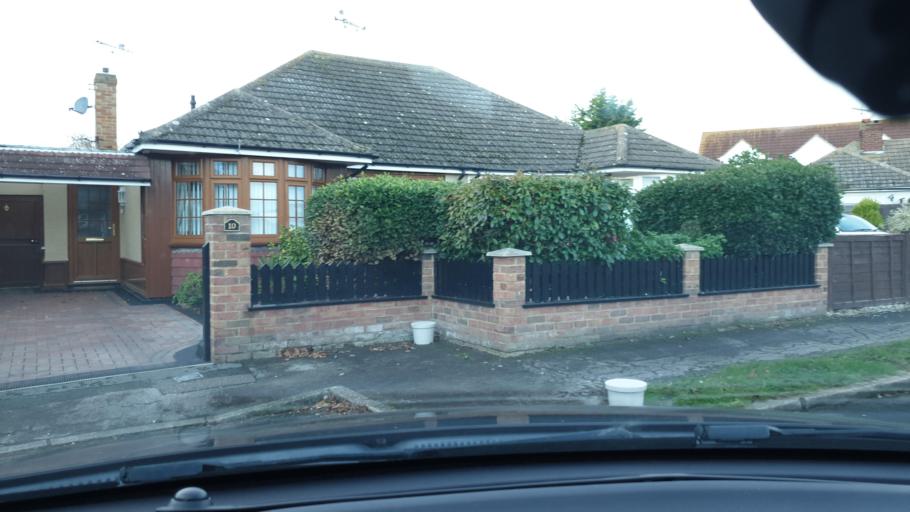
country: GB
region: England
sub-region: Essex
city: Clacton-on-Sea
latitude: 51.8082
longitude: 1.1703
